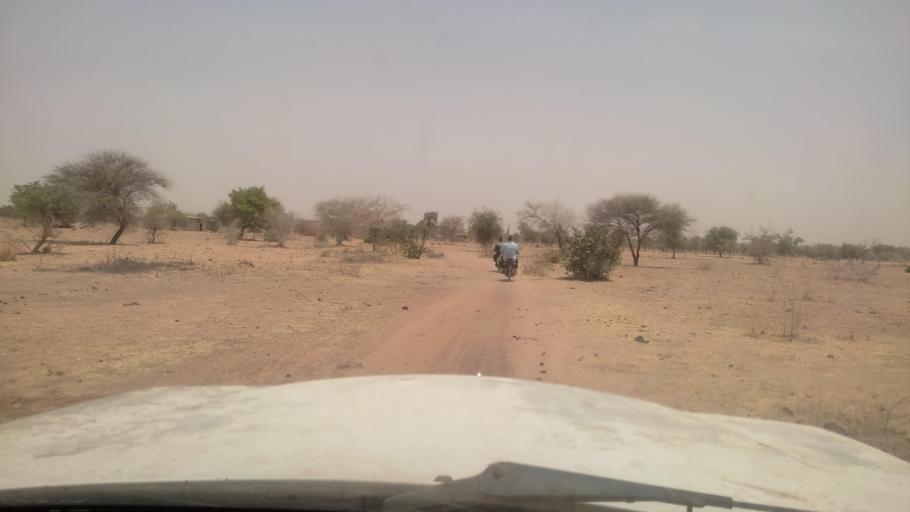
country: BF
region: Est
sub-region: Gnagna Province
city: Bogande
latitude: 13.0034
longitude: -0.0941
